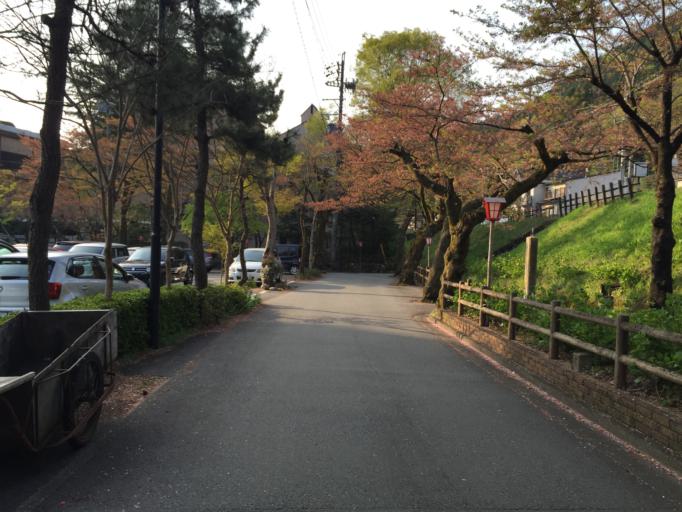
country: JP
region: Gifu
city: Gujo
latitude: 35.8052
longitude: 137.2404
